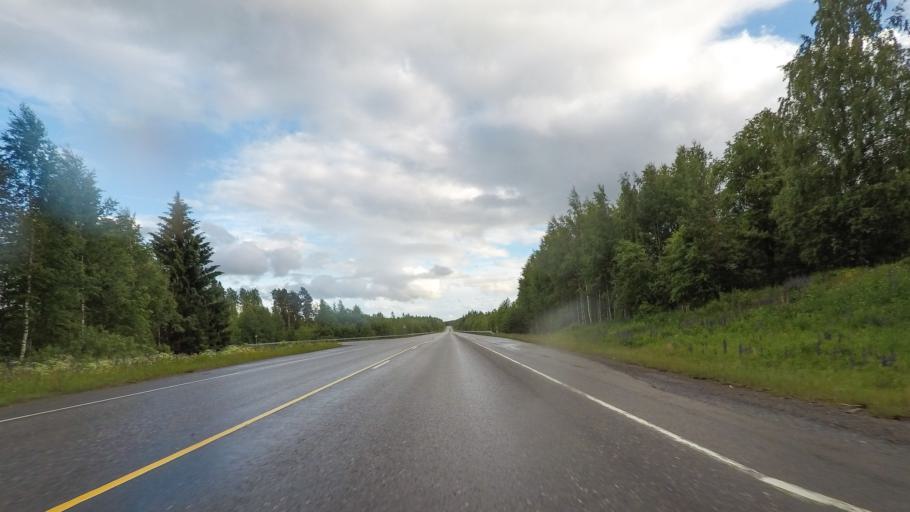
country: FI
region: Paijanne Tavastia
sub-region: Lahti
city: Heinola
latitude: 61.3279
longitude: 26.0408
